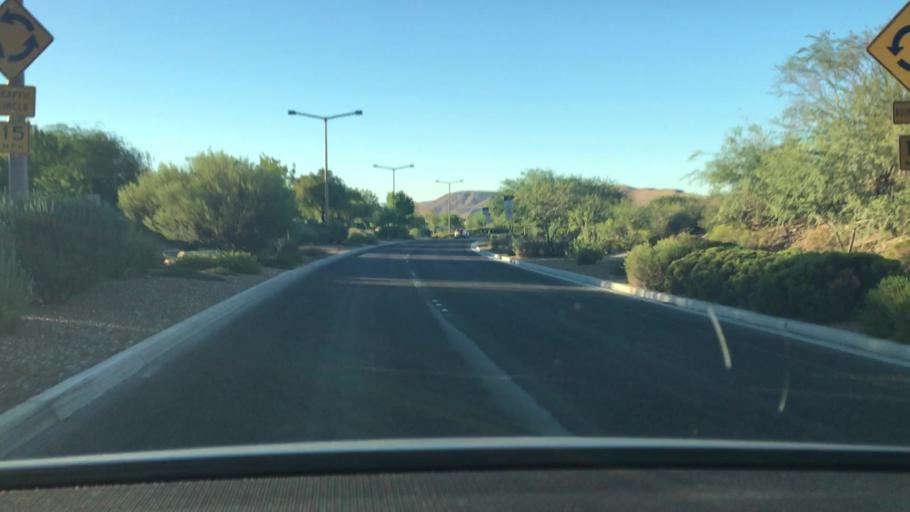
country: US
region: Nevada
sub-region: Clark County
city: Summerlin South
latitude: 36.1215
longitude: -115.3353
